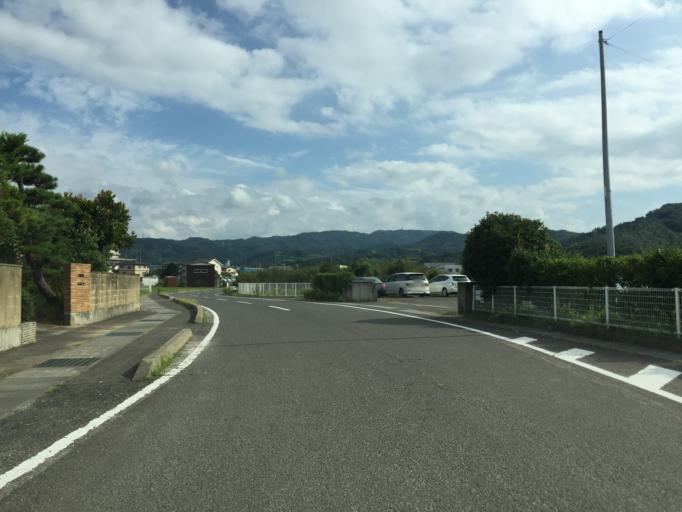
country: JP
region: Fukushima
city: Fukushima-shi
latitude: 37.7742
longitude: 140.5076
